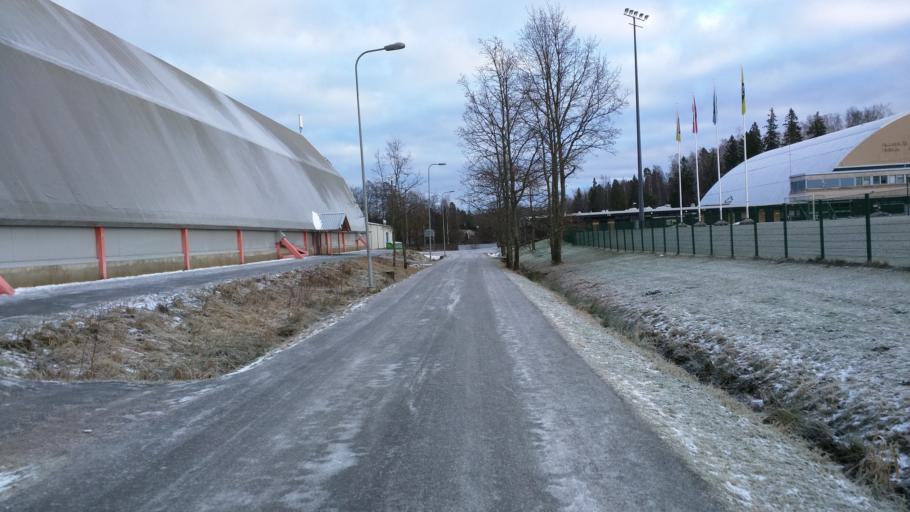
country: FI
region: Uusimaa
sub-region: Helsinki
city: Kauniainen
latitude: 60.2454
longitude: 24.7463
